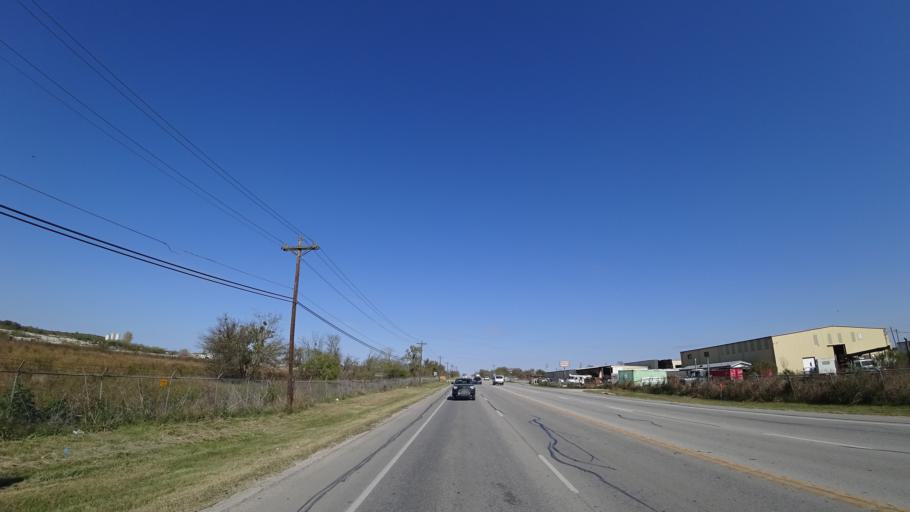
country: US
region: Texas
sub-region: Travis County
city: Onion Creek
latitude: 30.1543
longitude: -97.6959
